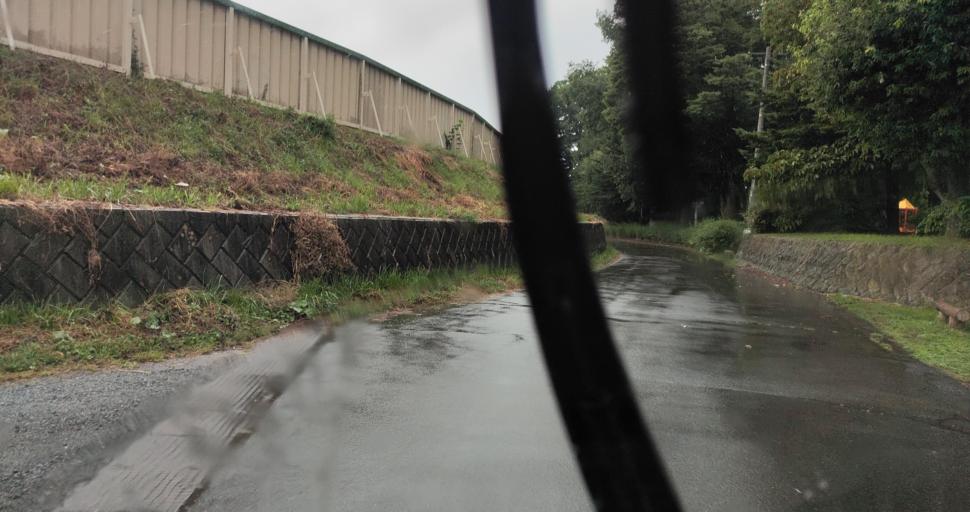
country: JP
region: Nagano
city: Saku
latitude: 36.2725
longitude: 138.4889
